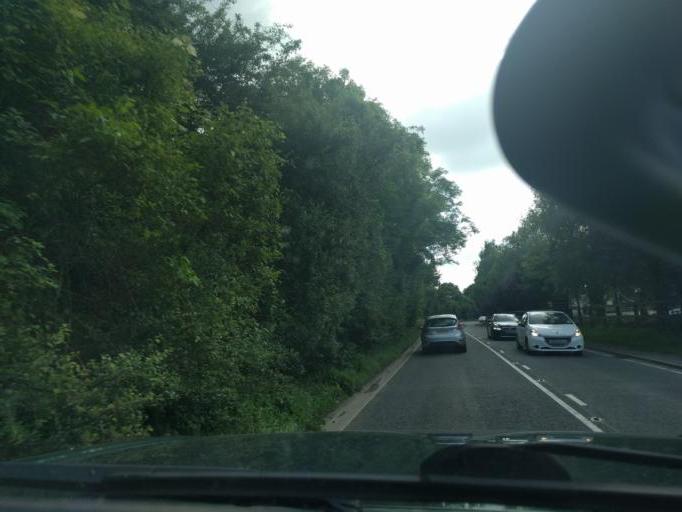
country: GB
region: England
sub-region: Wiltshire
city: Colerne
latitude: 51.4058
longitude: -2.2920
